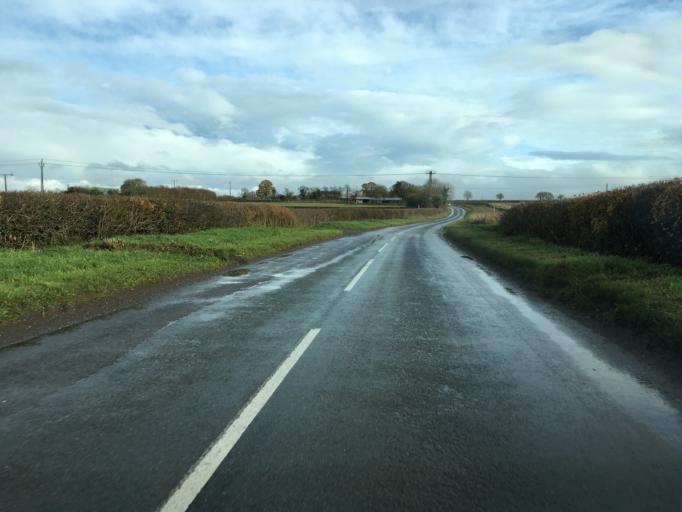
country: GB
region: England
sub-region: South Gloucestershire
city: Pucklechurch
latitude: 51.4896
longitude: -2.4165
